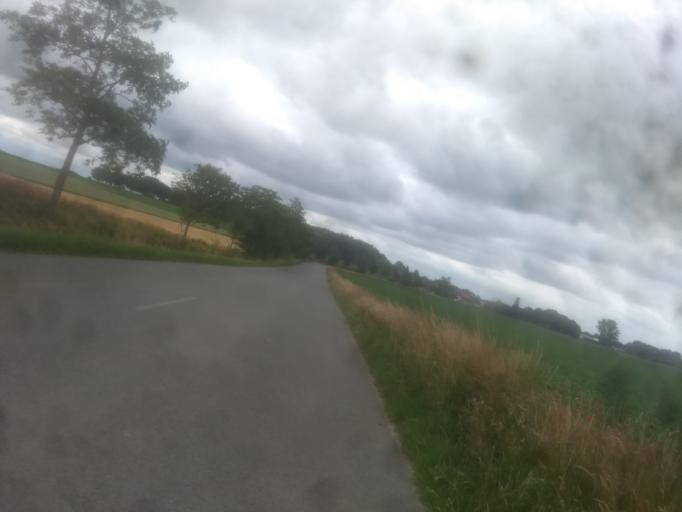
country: FR
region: Nord-Pas-de-Calais
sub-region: Departement du Pas-de-Calais
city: Thelus
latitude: 50.3326
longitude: 2.7935
